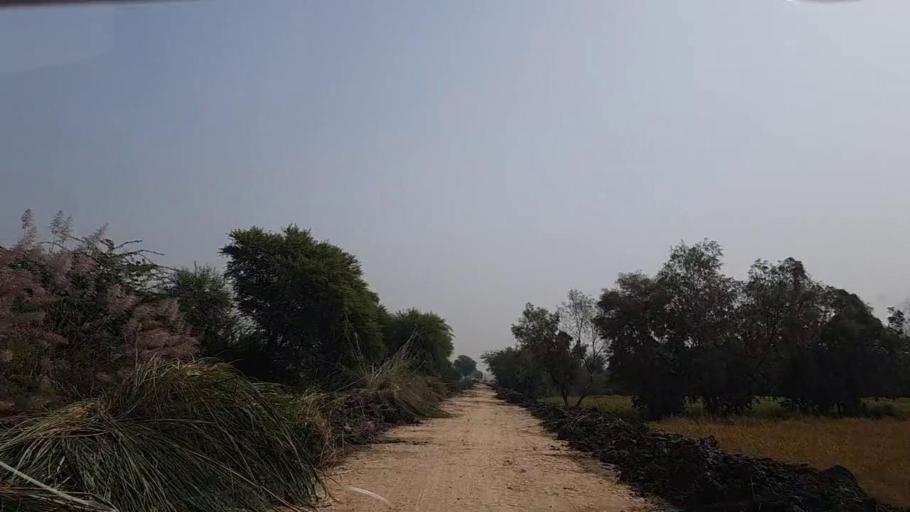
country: PK
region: Sindh
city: Shikarpur
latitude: 27.9198
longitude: 68.5821
